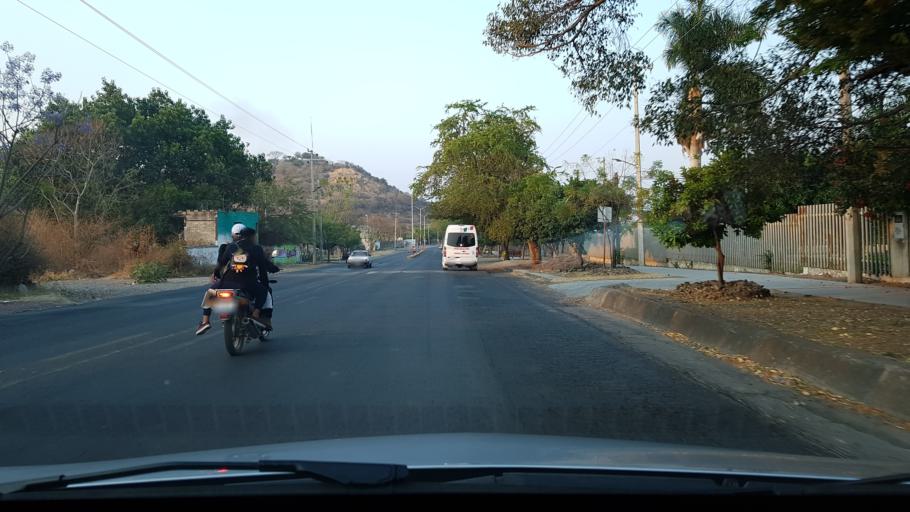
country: MX
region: Morelos
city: Jonacatepec de Leandro Valle
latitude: 18.6707
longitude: -98.8059
